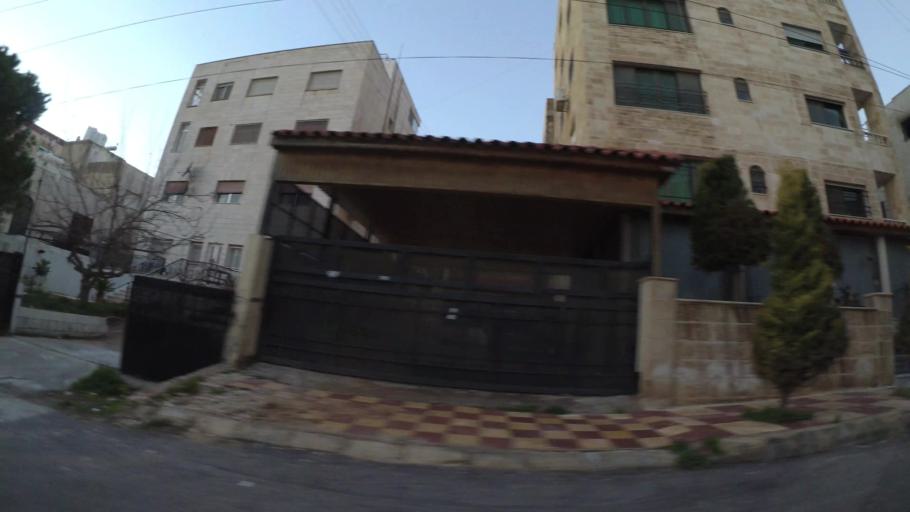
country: JO
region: Amman
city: Al Jubayhah
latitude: 31.9923
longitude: 35.8832
